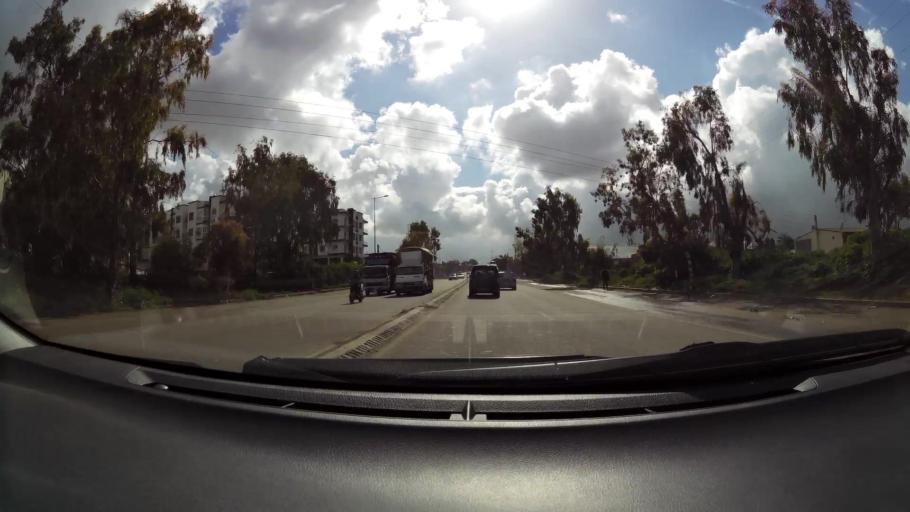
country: MA
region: Grand Casablanca
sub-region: Mediouna
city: Tit Mellil
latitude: 33.5666
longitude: -7.5060
